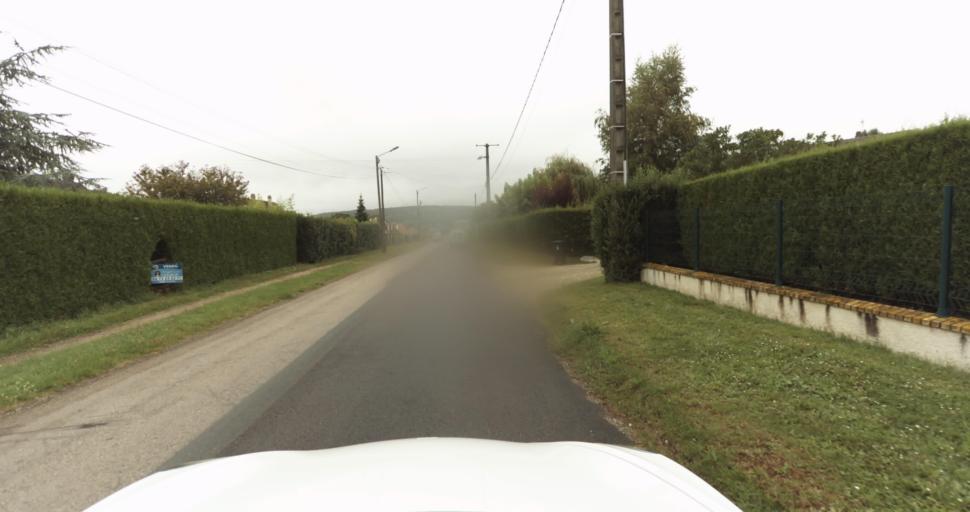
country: FR
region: Haute-Normandie
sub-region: Departement de l'Eure
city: Normanville
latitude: 49.0701
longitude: 1.1712
